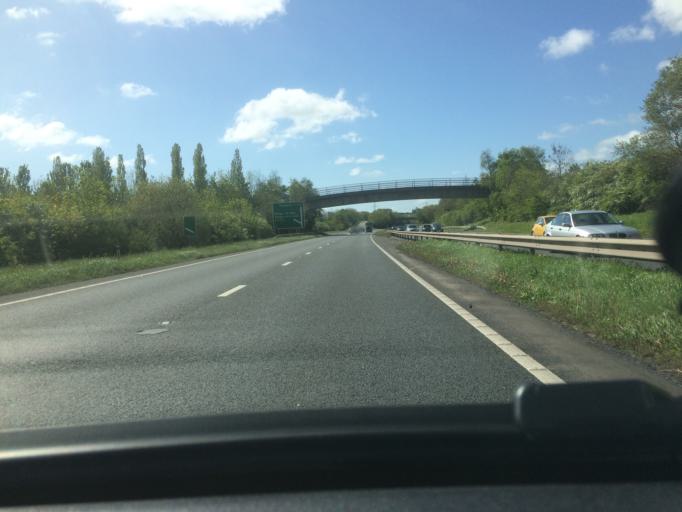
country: GB
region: Wales
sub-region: Wrexham
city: Ruabon
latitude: 53.0096
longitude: -3.0224
